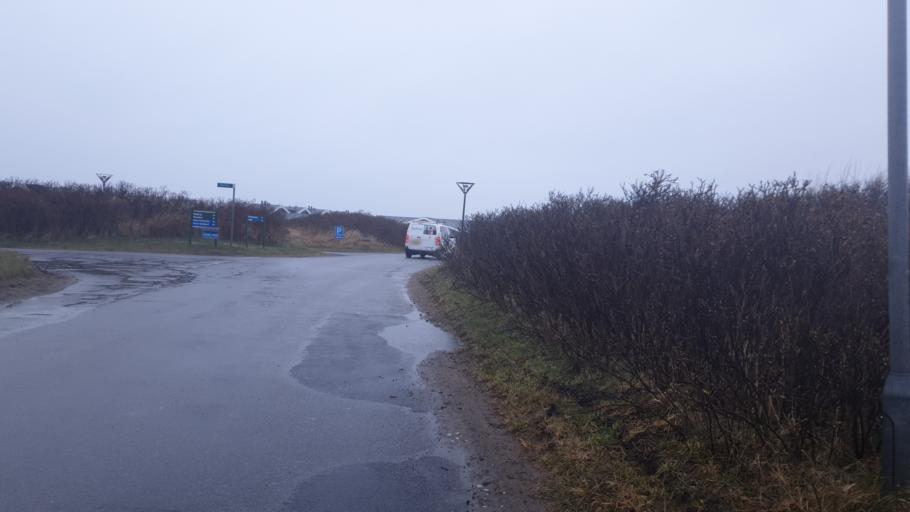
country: DK
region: North Denmark
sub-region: Hjorring Kommune
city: Hjorring
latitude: 57.4945
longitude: 9.8380
